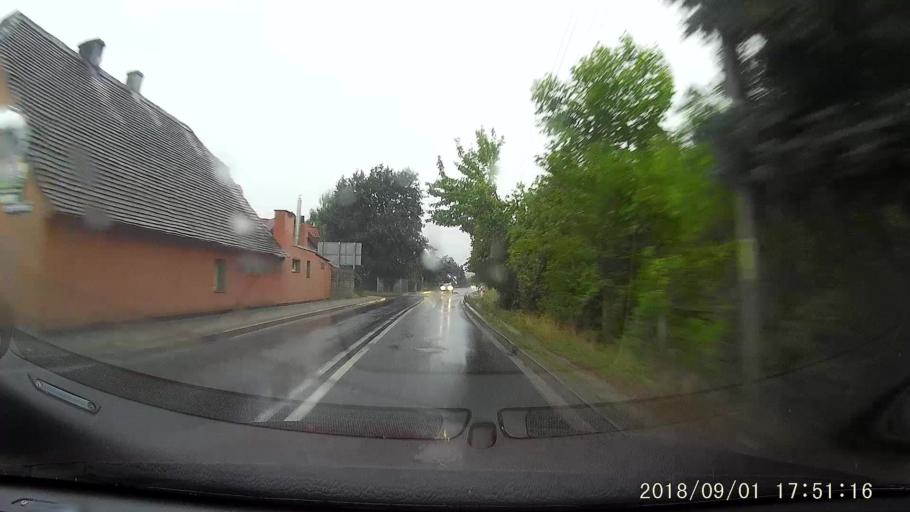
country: PL
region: Lubusz
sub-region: Powiat zaganski
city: Ilowa
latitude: 51.4986
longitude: 15.1928
